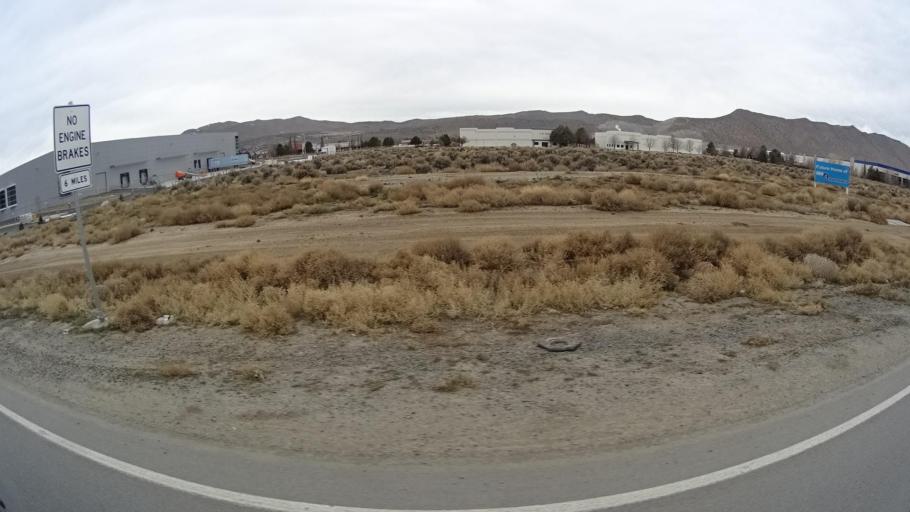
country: US
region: Nevada
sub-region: Washoe County
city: Spanish Springs
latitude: 39.6700
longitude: -119.7026
